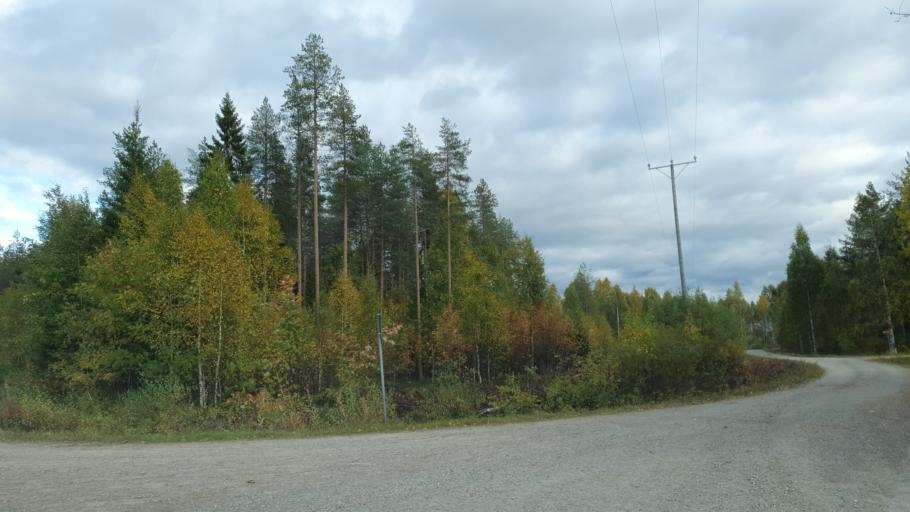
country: FI
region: Kainuu
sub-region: Kehys-Kainuu
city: Kuhmo
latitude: 63.9481
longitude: 29.8810
